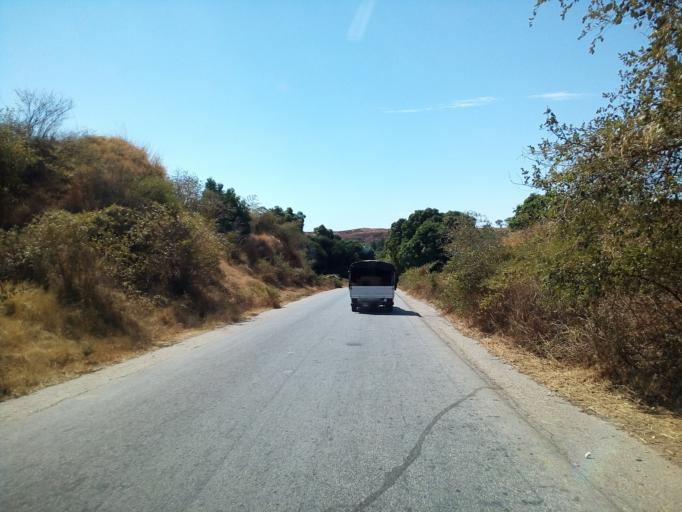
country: MG
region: Betsiboka
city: Maevatanana
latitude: -16.9139
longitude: 46.8696
